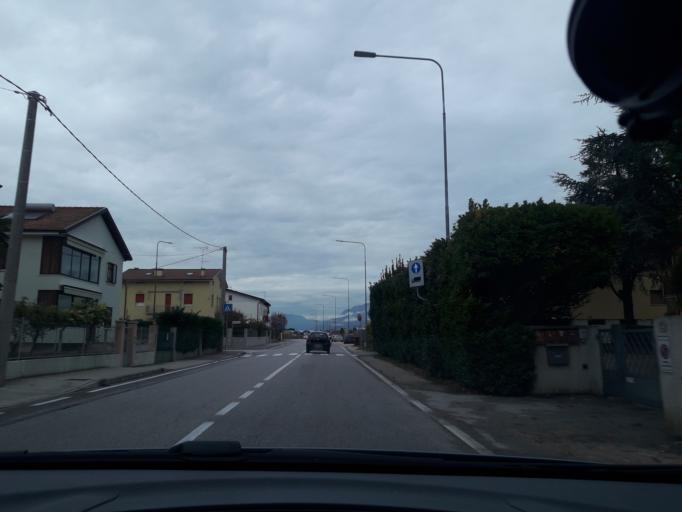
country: IT
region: Friuli Venezia Giulia
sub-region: Provincia di Udine
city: Colugna
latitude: 46.0877
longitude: 13.2151
